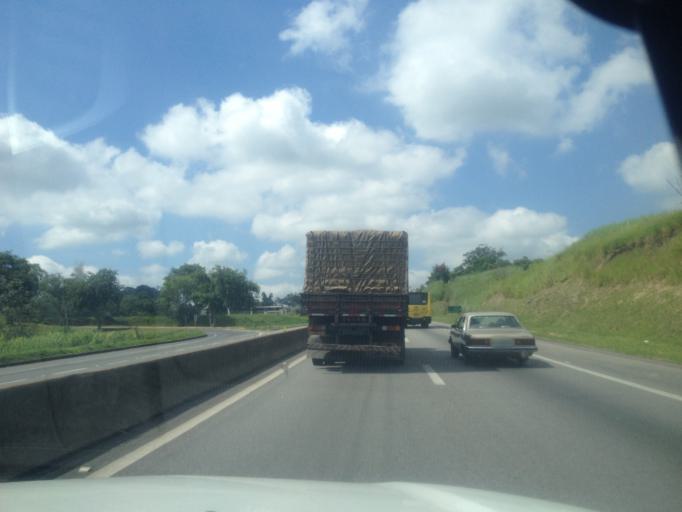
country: BR
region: Rio de Janeiro
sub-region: Volta Redonda
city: Volta Redonda
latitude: -22.5907
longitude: -44.0799
